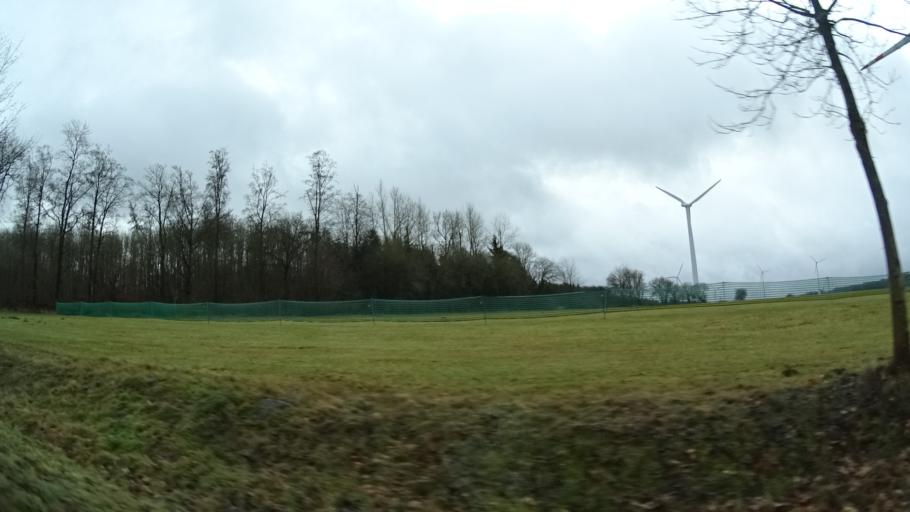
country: DE
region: Hesse
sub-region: Regierungsbezirk Giessen
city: Lautertal
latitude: 50.6164
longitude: 9.2799
